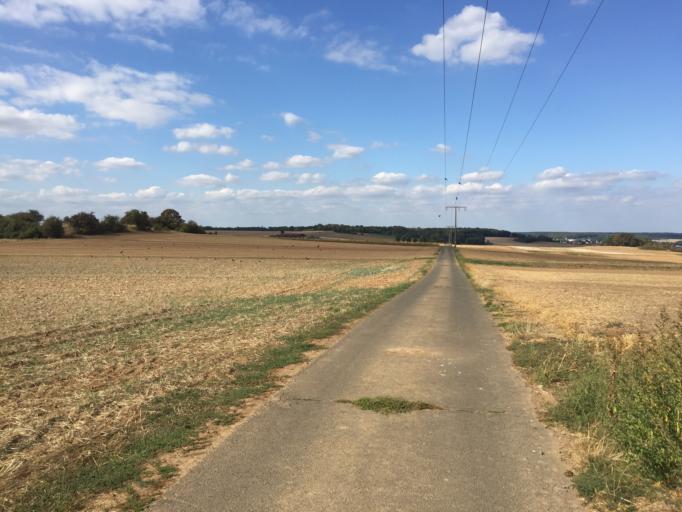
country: DE
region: Hesse
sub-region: Regierungsbezirk Giessen
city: Lich
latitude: 50.4892
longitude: 8.8300
